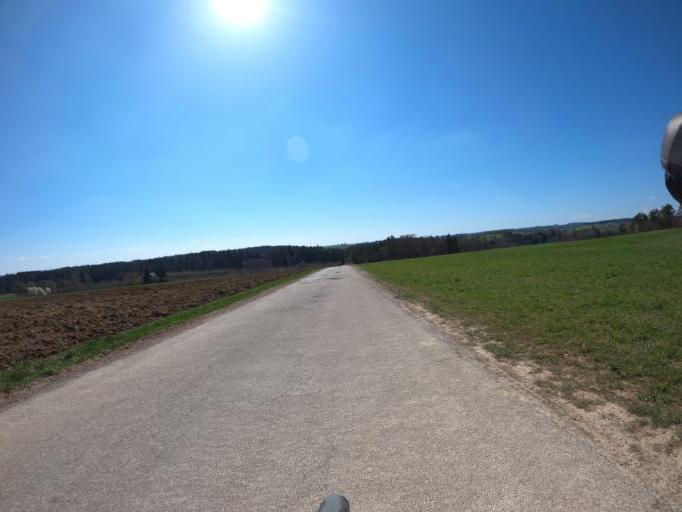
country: DE
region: Baden-Wuerttemberg
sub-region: Karlsruhe Region
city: Horb am Neckar
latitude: 48.4207
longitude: 8.6875
